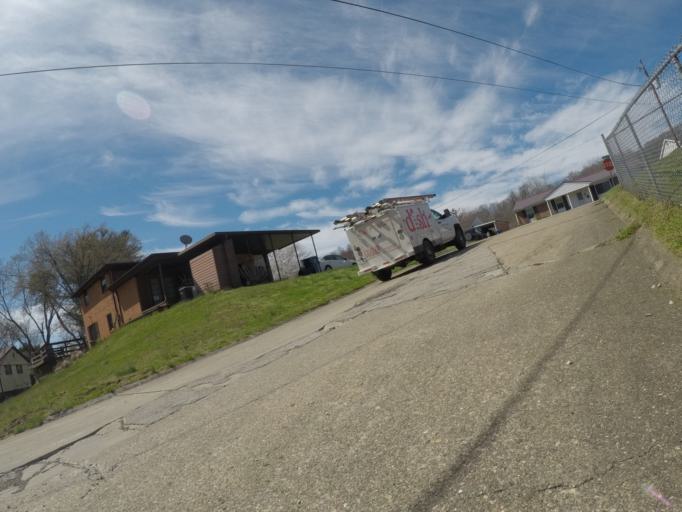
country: US
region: West Virginia
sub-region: Cabell County
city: Pea Ridge
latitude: 38.4053
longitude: -82.3166
